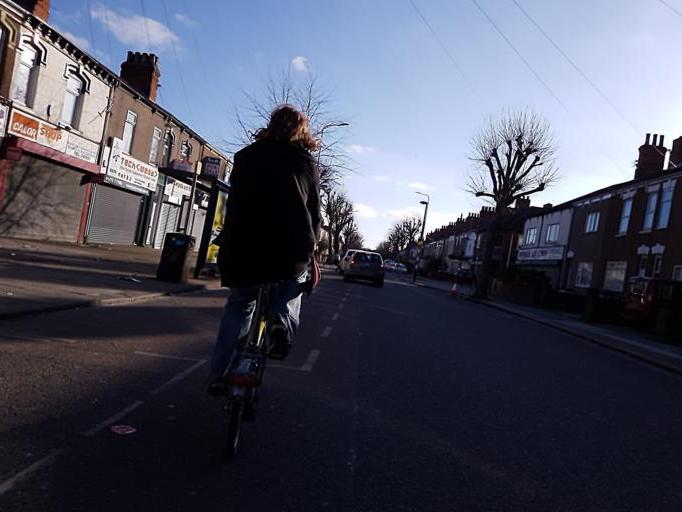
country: GB
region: England
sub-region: North East Lincolnshire
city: Grimsby
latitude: 53.5627
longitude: -0.0760
